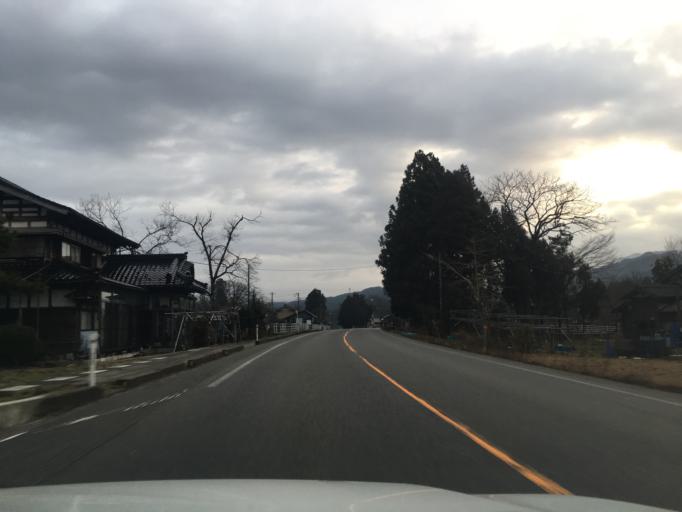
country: JP
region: Niigata
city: Murakami
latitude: 38.3033
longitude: 139.5395
